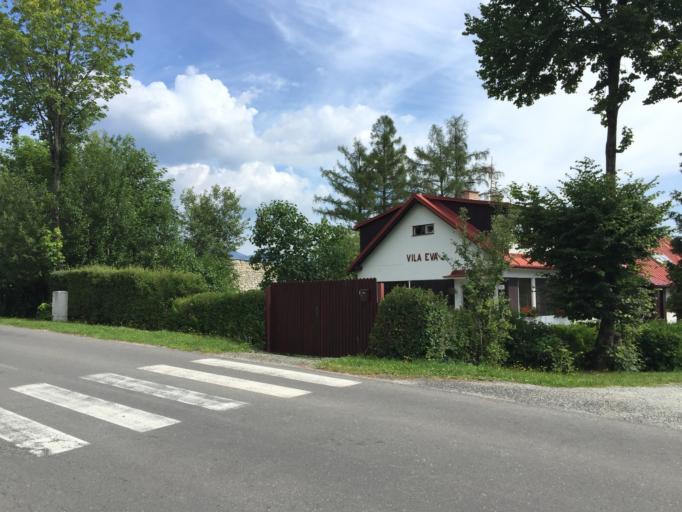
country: SK
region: Presovsky
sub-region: Okres Poprad
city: Vysoke Tatry
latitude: 49.1275
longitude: 20.2502
